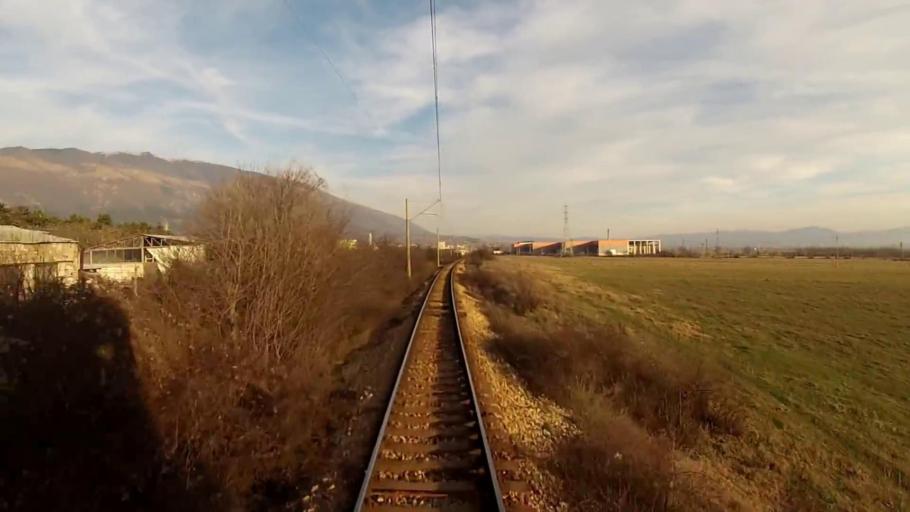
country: BG
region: Plovdiv
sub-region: Obshtina Karlovo
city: Karlovo
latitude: 42.6314
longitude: 24.7837
